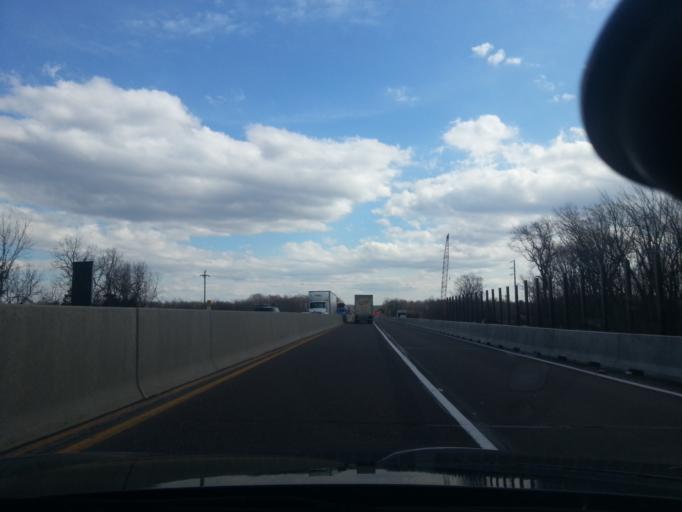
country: US
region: Pennsylvania
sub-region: Montgomery County
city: Kulpsville
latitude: 40.2387
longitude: -75.3405
